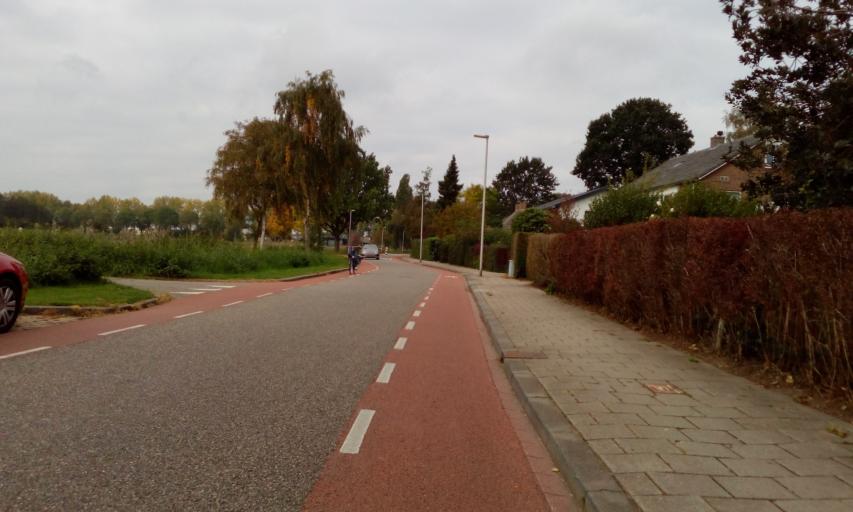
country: NL
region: South Holland
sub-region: Gemeente Albrandswaard
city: Rhoon
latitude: 51.8561
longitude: 4.4134
